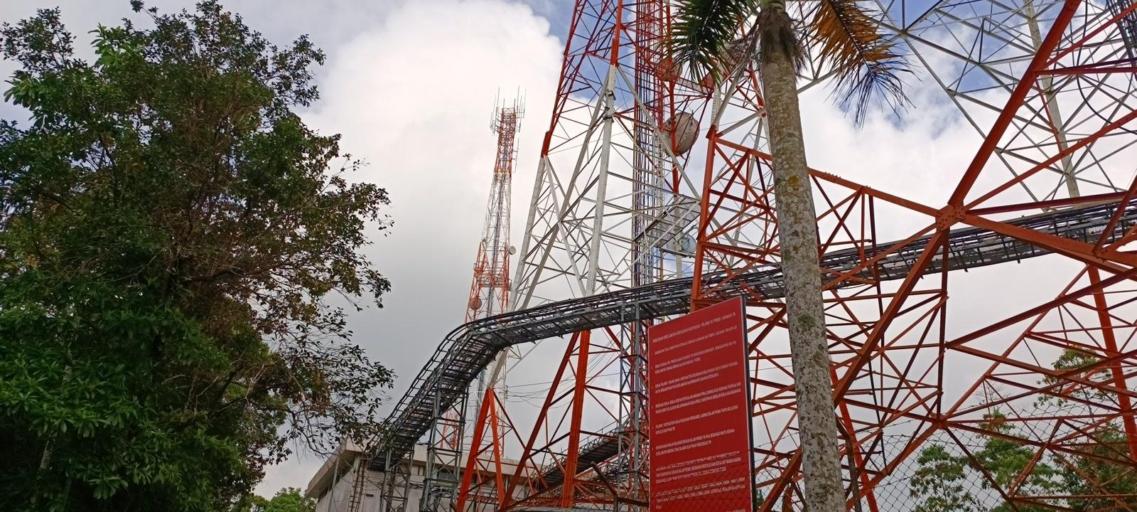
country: MY
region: Penang
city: Bukit Mertajam
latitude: 5.3669
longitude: 100.4838
